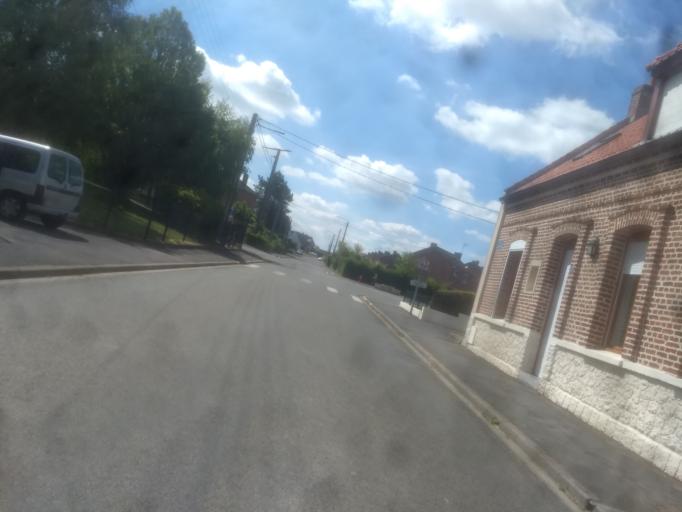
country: FR
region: Nord-Pas-de-Calais
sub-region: Departement du Pas-de-Calais
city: Agny
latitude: 50.2565
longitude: 2.7584
